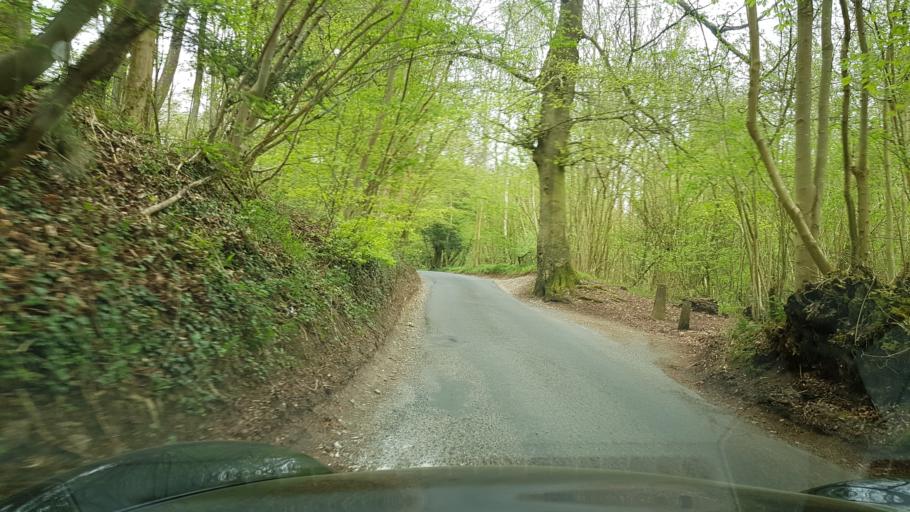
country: GB
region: England
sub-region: Surrey
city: East Horsley
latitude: 51.2294
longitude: -0.4054
